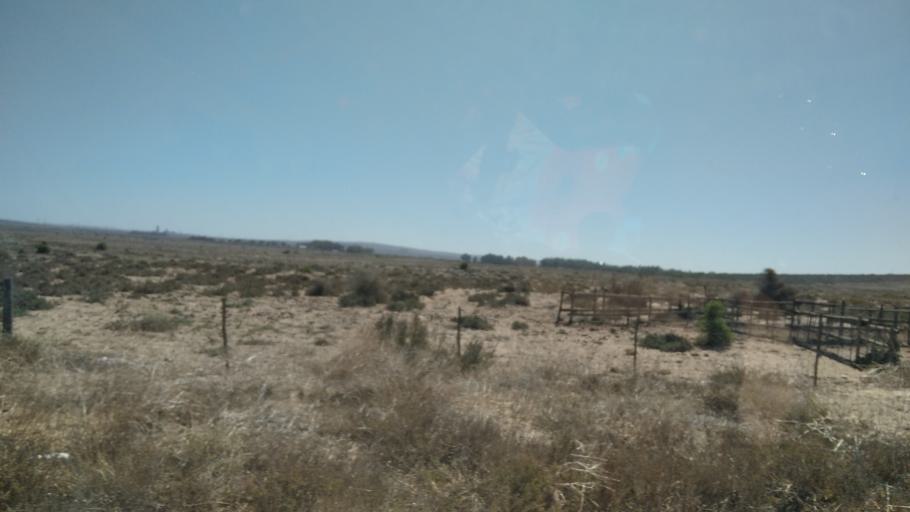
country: ZA
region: Western Cape
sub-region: West Coast District Municipality
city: Vredenburg
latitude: -33.0166
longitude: 18.1131
